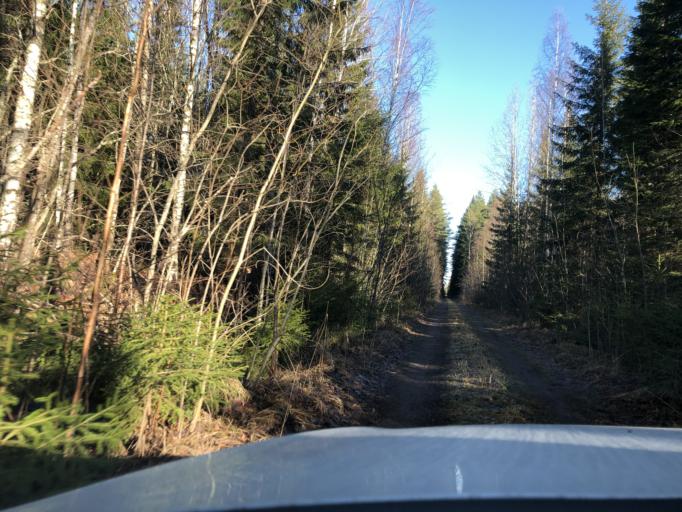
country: SE
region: Gaevleborg
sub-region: Gavle Kommun
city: Hedesunda
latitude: 60.2972
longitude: 16.8980
